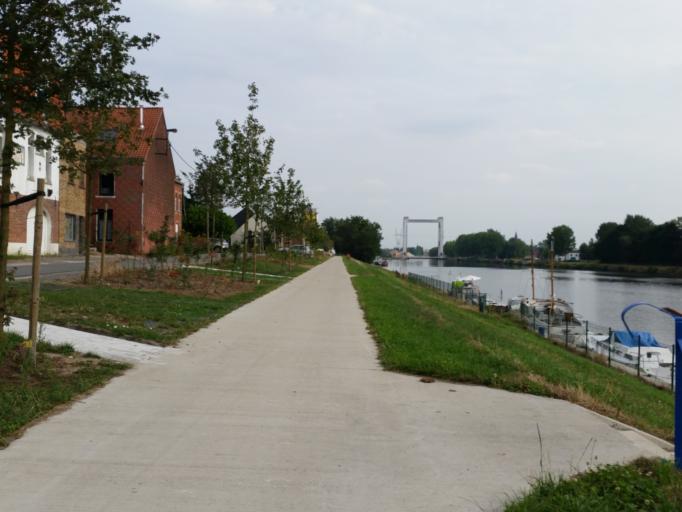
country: BE
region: Flanders
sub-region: Provincie Vlaams-Brabant
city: Vilvoorde
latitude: 50.9554
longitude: 4.4091
